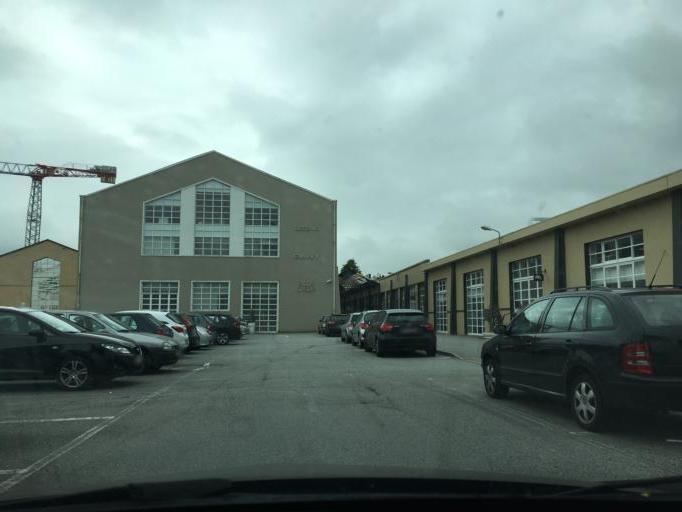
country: PT
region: Porto
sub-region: Maia
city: Leca do Bailio
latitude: 41.2162
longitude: -8.6229
